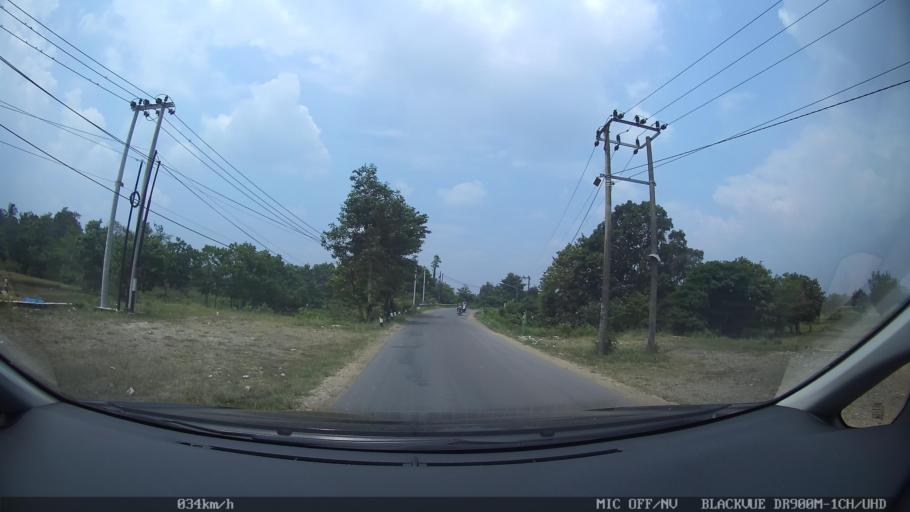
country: ID
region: Lampung
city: Pringsewu
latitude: -5.3538
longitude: 105.0137
